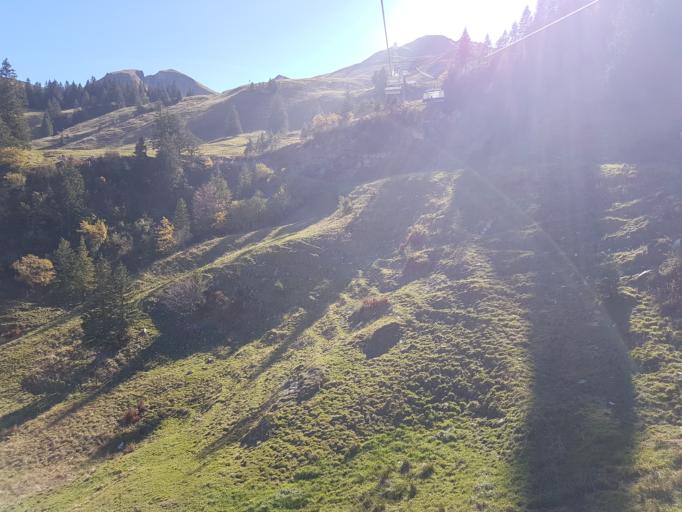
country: CH
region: Schwyz
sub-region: Bezirk Schwyz
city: Ibach
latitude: 46.9704
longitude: 8.6721
